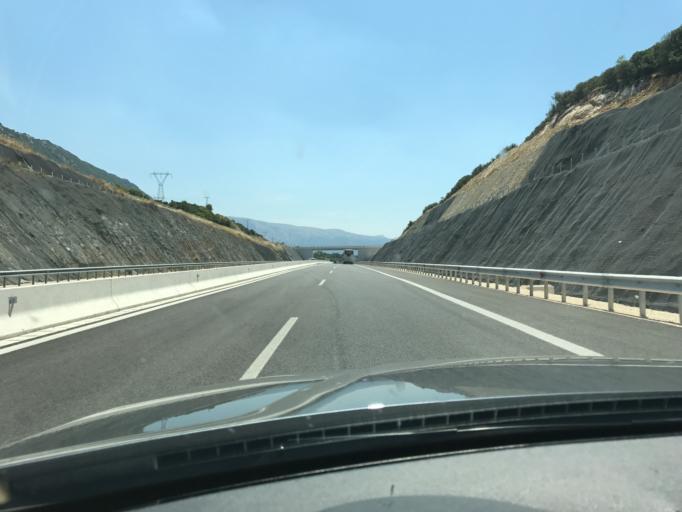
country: GR
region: Epirus
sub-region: Nomos Ioanninon
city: Agia Kyriaki
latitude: 39.4922
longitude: 20.8892
